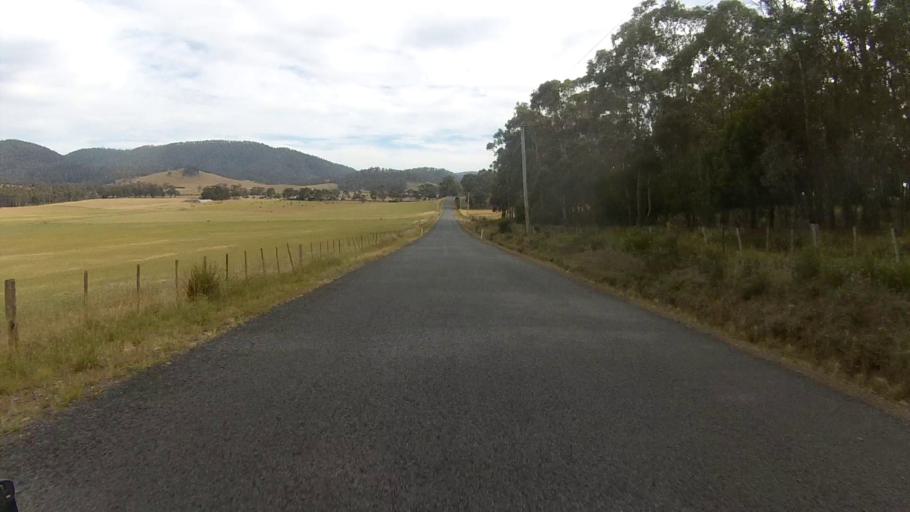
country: AU
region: Tasmania
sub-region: Sorell
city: Sorell
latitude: -42.8007
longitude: 147.7935
